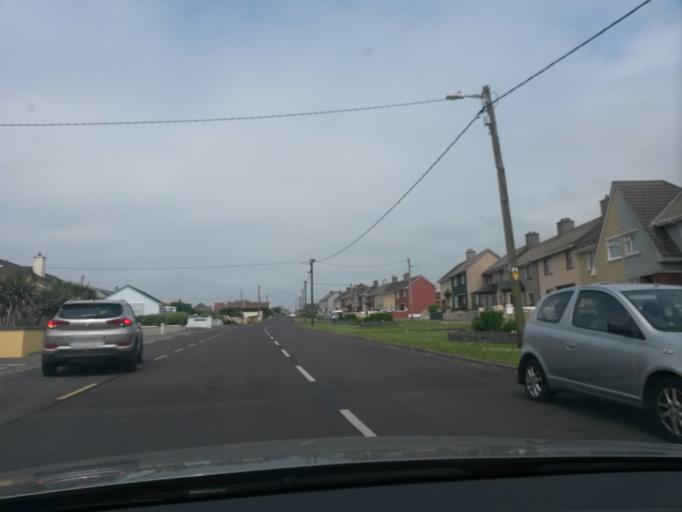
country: IE
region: Munster
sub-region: Ciarrai
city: Ballybunnion
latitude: 52.5188
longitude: -9.6736
